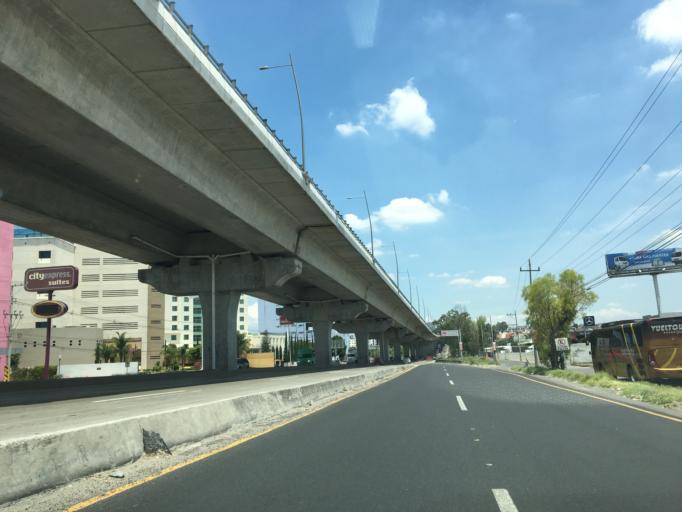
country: MX
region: Puebla
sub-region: Cuautlancingo
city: Sanctorum
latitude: 19.0991
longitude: -98.2328
